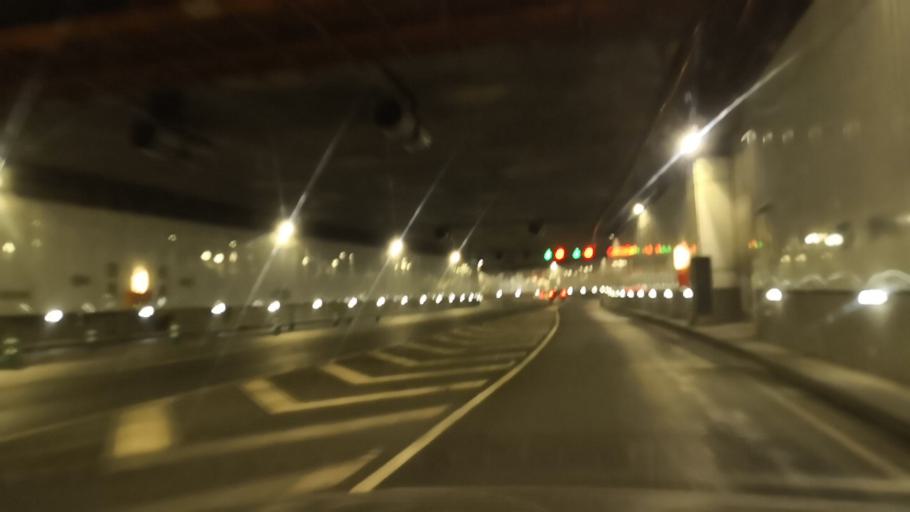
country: ES
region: Galicia
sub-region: Provincia da Coruna
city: A Coruna
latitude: 43.3672
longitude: -8.3943
